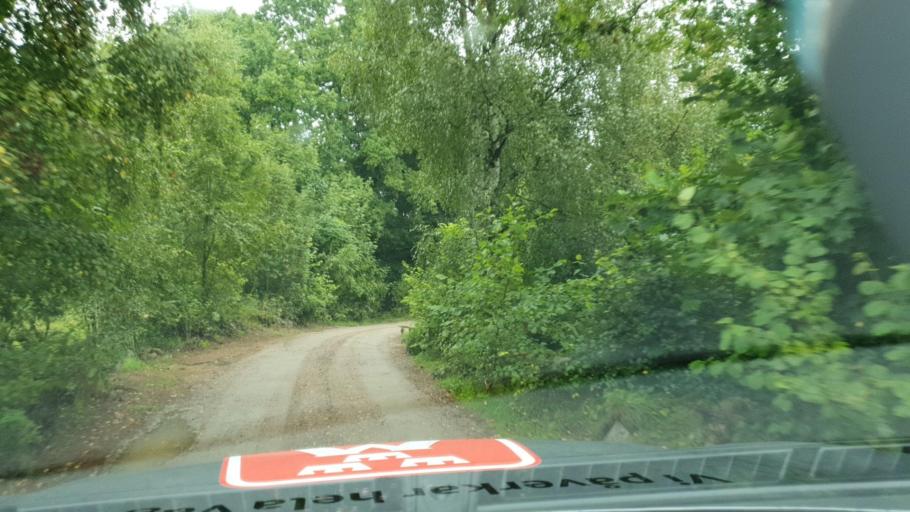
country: SE
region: Skane
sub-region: Kristianstads Kommun
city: Degeberga
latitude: 55.7716
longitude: 13.9238
